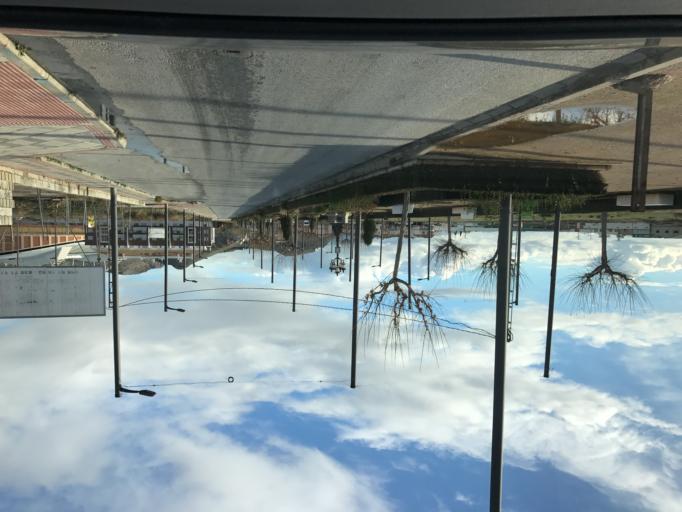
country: ES
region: Andalusia
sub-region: Provincia de Granada
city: Atarfe
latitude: 37.2219
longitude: -3.6983
